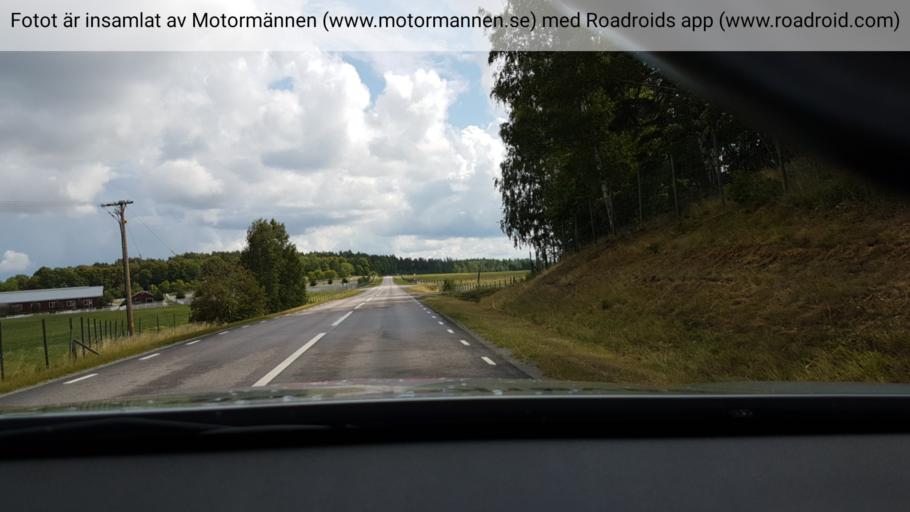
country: SE
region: Stockholm
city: Stenhamra
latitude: 59.3468
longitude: 17.6296
